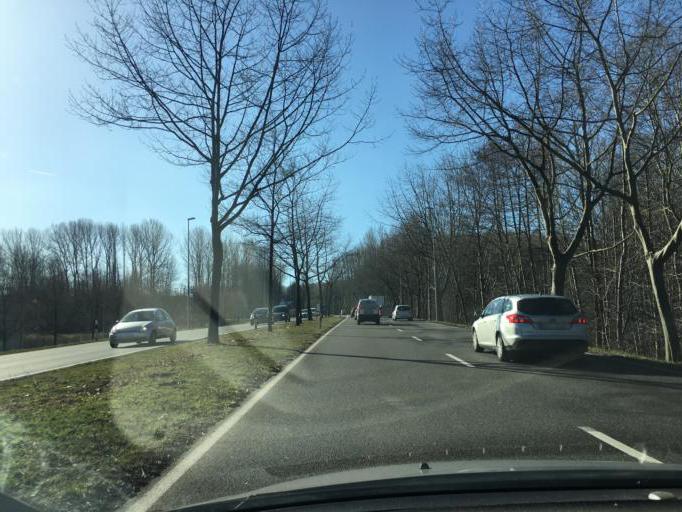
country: DE
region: Saxony
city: Neukirchen
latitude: 50.8094
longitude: 12.8760
